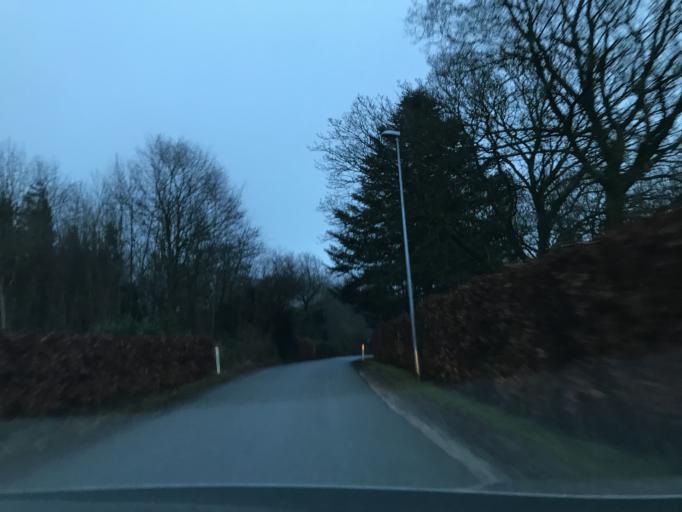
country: DK
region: South Denmark
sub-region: Vejle Kommune
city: Brejning
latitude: 55.6873
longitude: 9.7631
